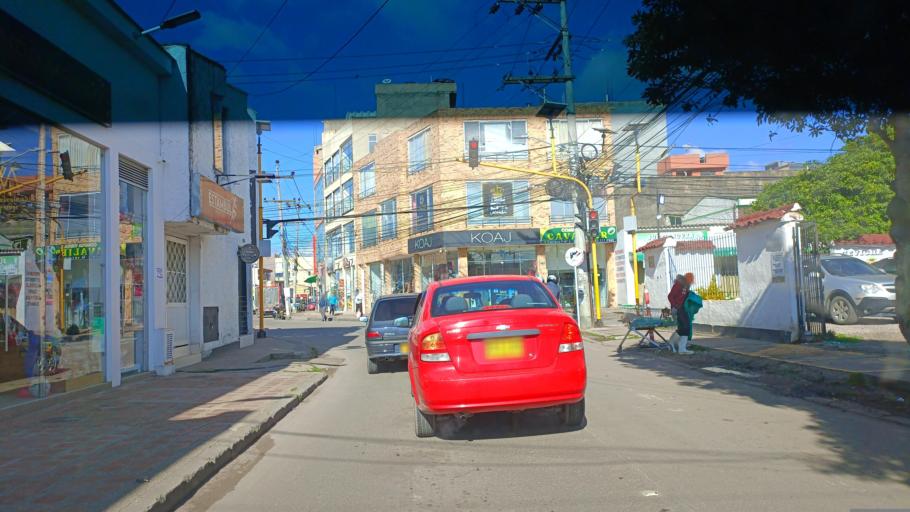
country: CO
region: Cundinamarca
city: Cajica
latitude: 4.9183
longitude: -74.0272
